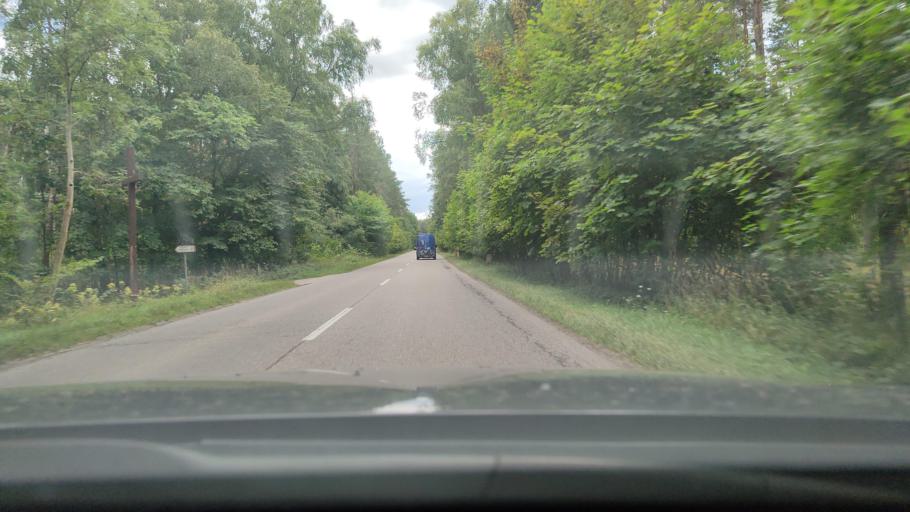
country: PL
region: Pomeranian Voivodeship
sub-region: Powiat wejherowski
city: Orle
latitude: 54.6543
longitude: 18.2104
